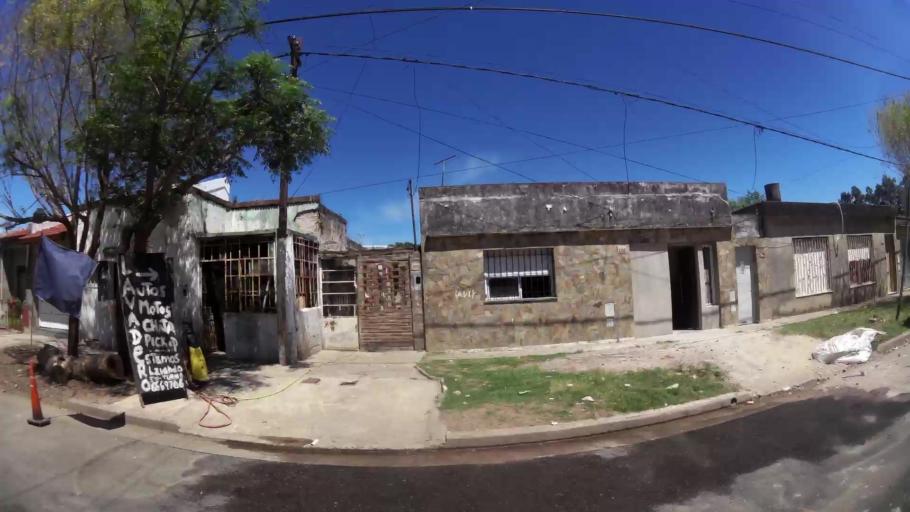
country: AR
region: Santa Fe
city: Perez
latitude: -32.9553
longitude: -60.7108
